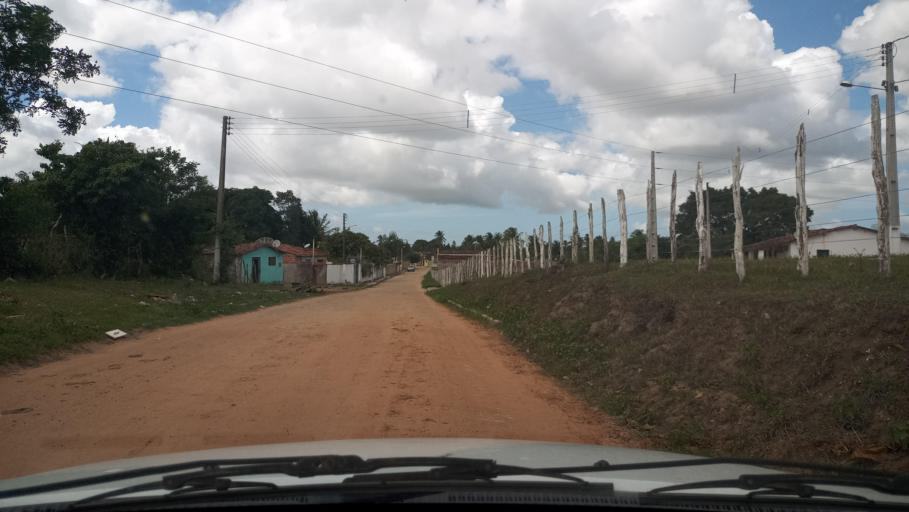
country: BR
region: Rio Grande do Norte
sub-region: Goianinha
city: Goianinha
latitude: -6.2643
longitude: -35.2368
